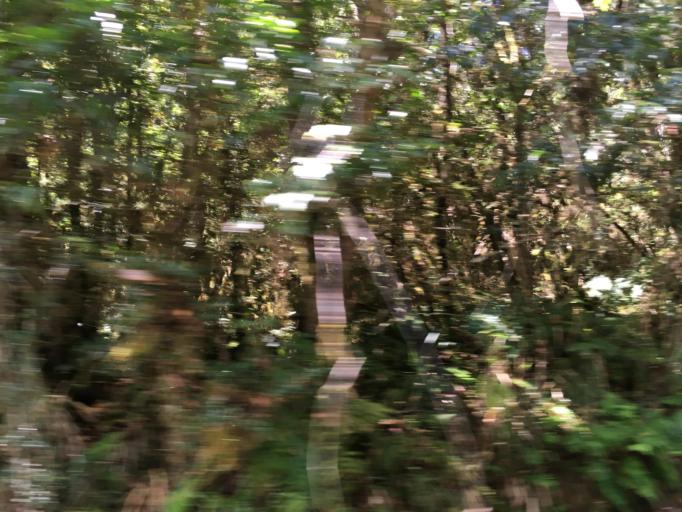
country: TW
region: Taiwan
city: Daxi
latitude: 24.5518
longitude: 121.3968
